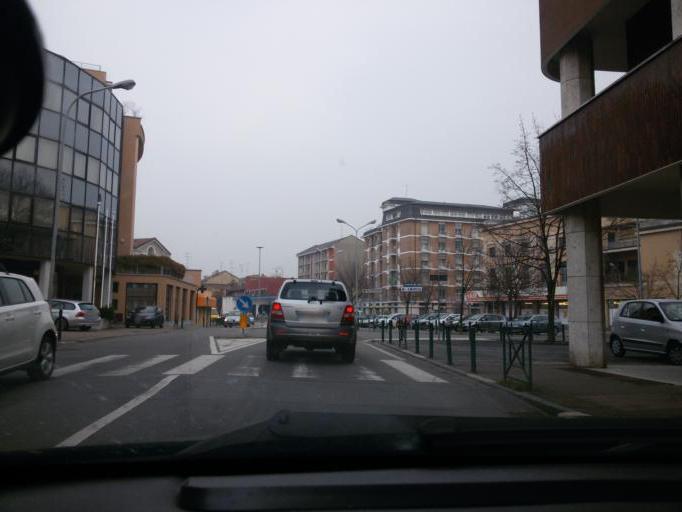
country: IT
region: Piedmont
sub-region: Provincia di Vercelli
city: Vercelli
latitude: 45.3227
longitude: 8.4150
